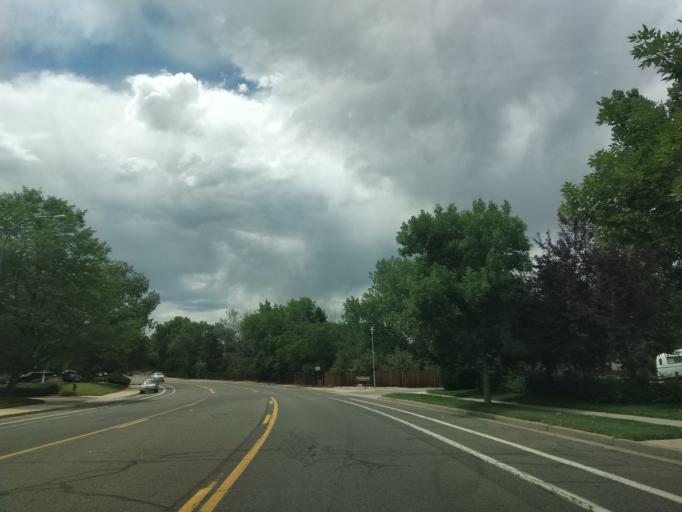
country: US
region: Colorado
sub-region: Jefferson County
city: Lakewood
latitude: 39.6916
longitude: -105.1198
